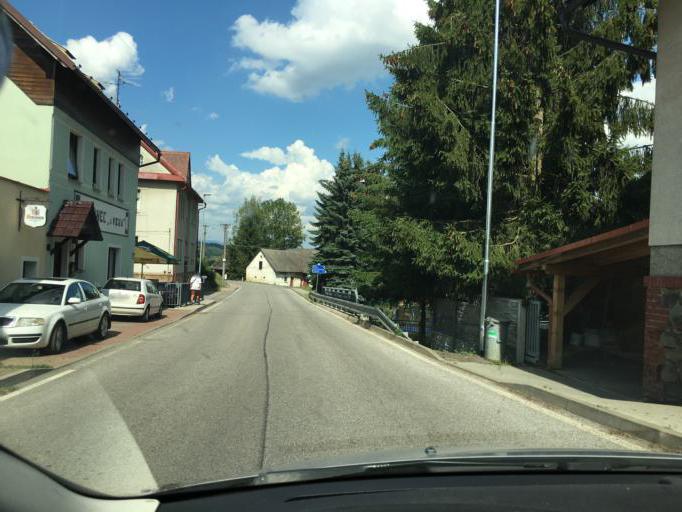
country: CZ
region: Liberecky
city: Semily
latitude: 50.6023
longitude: 15.2995
